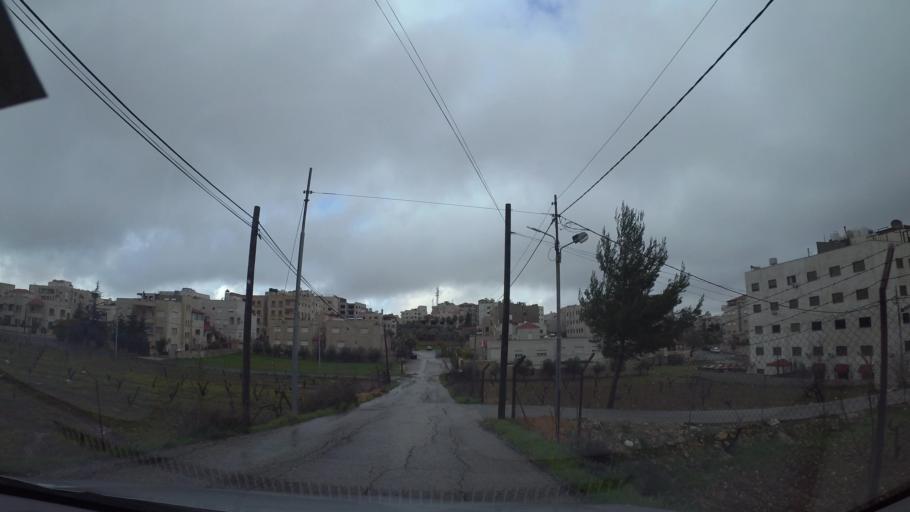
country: JO
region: Amman
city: Al Jubayhah
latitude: 32.0318
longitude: 35.8587
